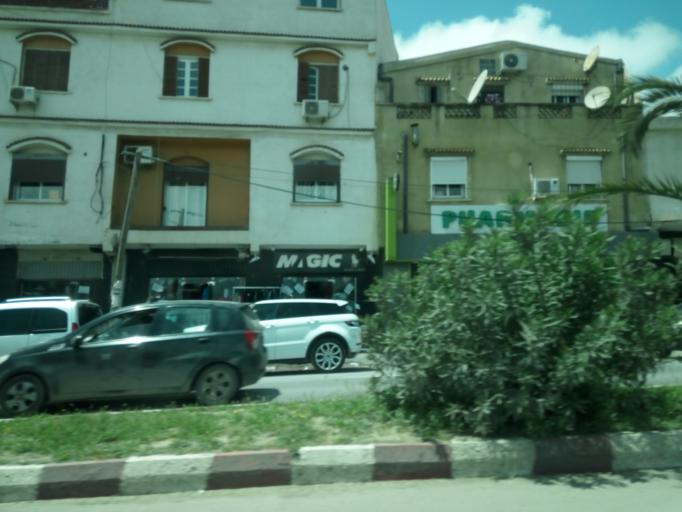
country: DZ
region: Tipaza
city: Saoula
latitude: 36.7303
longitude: 2.9923
